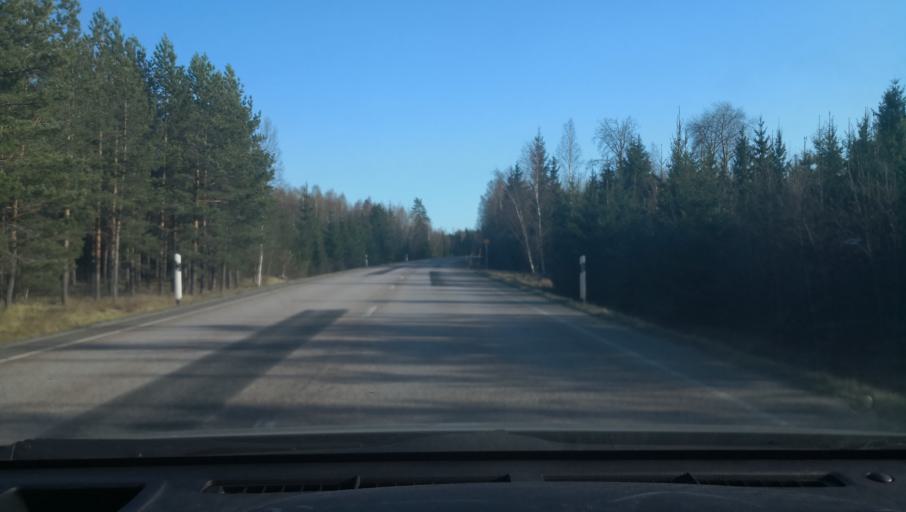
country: SE
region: Uppsala
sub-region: Heby Kommun
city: Heby
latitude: 59.9793
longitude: 16.8357
